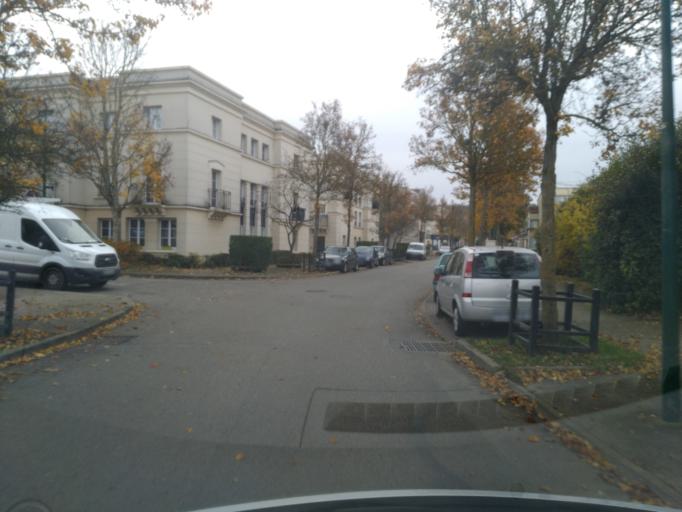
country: FR
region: Ile-de-France
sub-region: Departement des Yvelines
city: Plaisir
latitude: 48.8211
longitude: 1.9658
